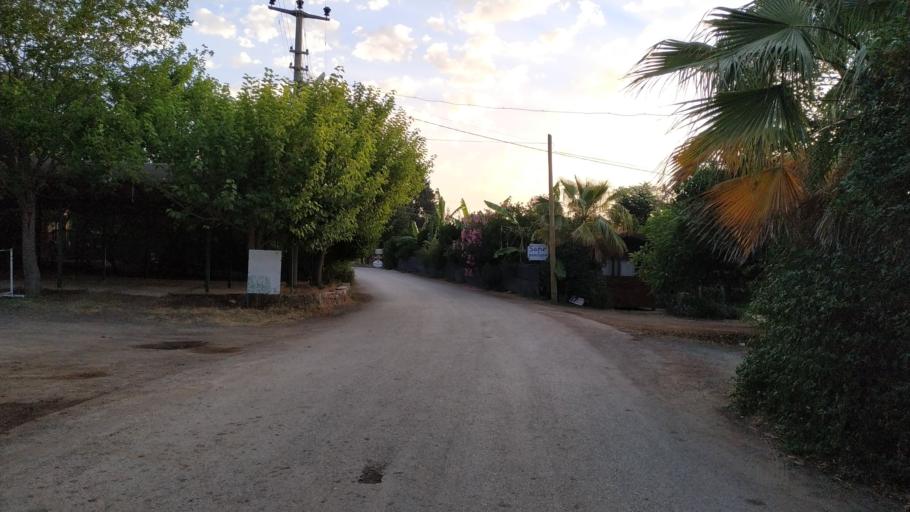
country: TR
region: Antalya
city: Tekirova
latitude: 36.4099
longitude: 30.4747
